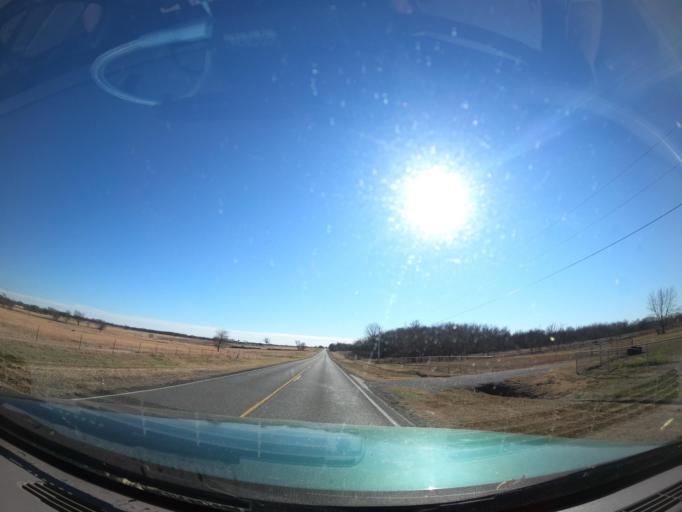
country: US
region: Oklahoma
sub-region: Muskogee County
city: Haskell
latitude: 35.6810
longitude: -95.6422
